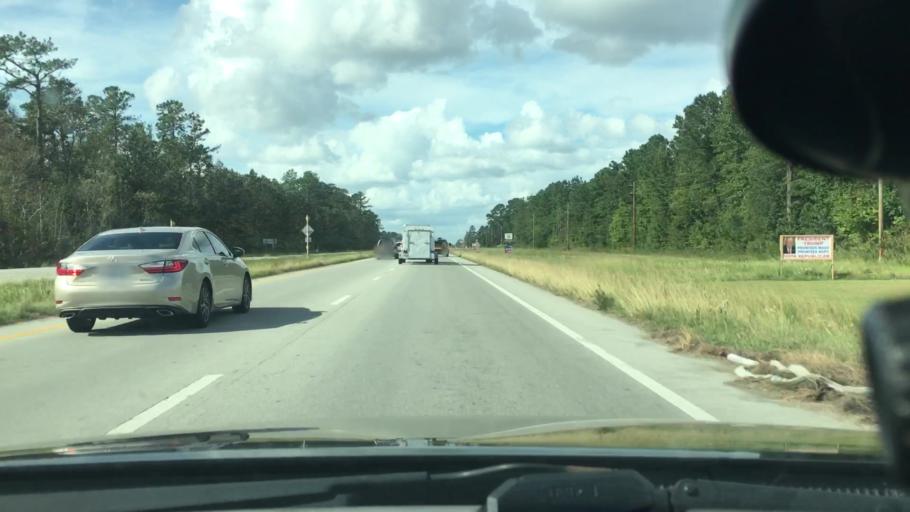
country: US
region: North Carolina
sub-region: Craven County
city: James City
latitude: 35.0511
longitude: -77.0147
